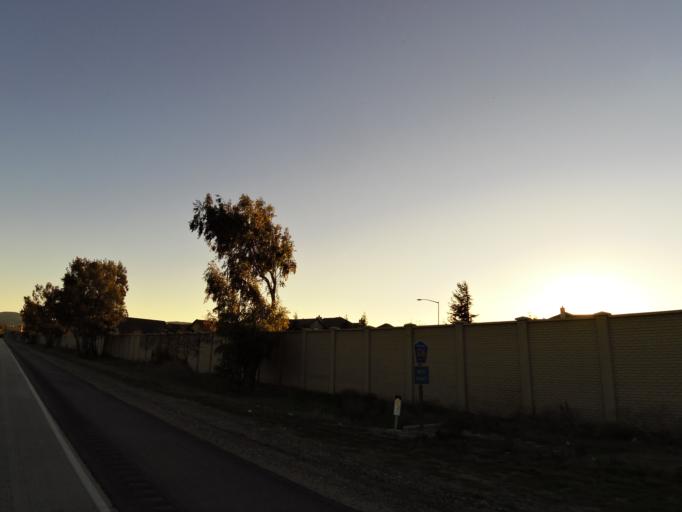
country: US
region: California
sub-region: Monterey County
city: Greenfield
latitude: 36.3184
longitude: -121.2353
